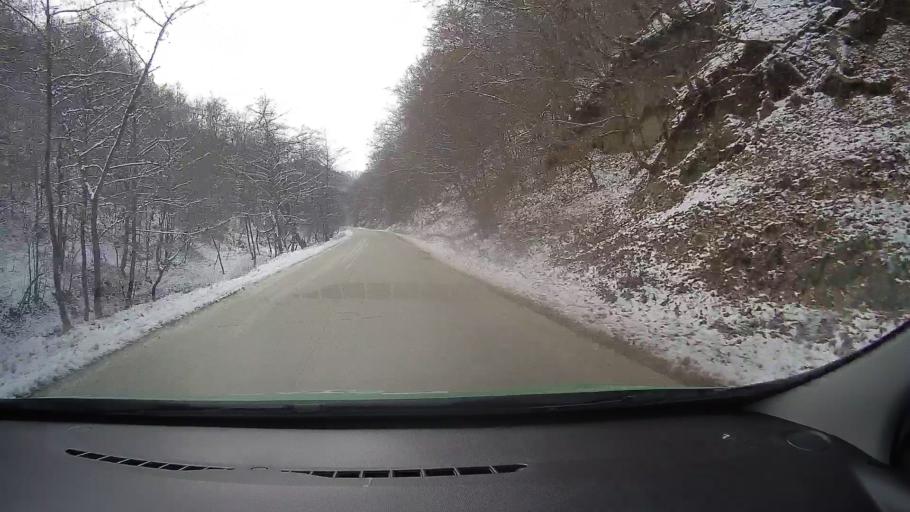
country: RO
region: Alba
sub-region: Oras Zlatna
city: Zlatna
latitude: 46.1061
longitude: 23.1938
